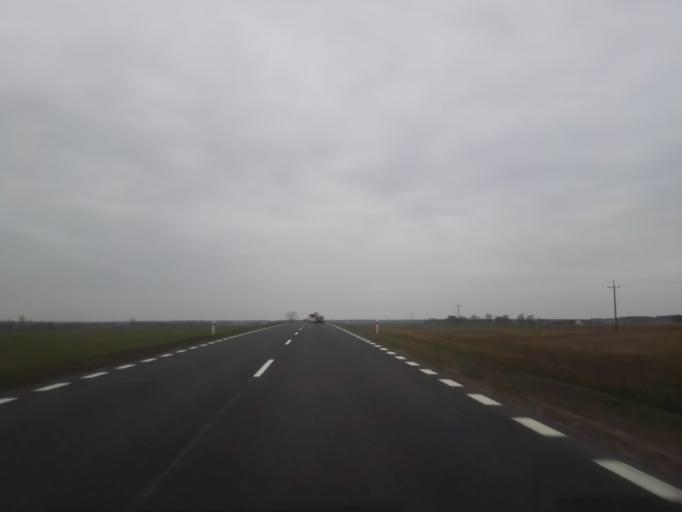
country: PL
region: Podlasie
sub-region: Powiat kolnenski
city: Stawiski
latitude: 53.4114
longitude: 22.1620
